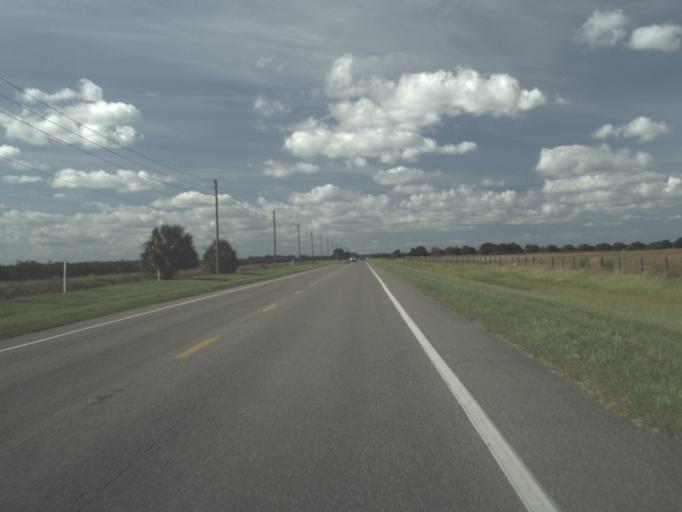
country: US
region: Florida
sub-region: DeSoto County
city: Nocatee
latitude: 27.0270
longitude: -81.7667
